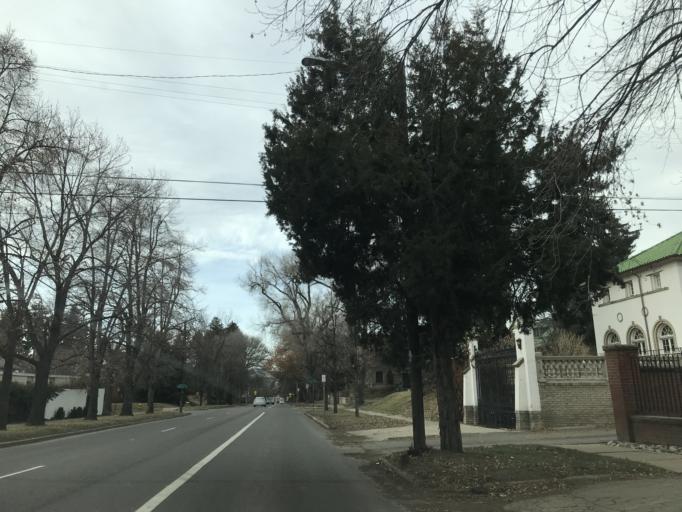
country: US
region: Colorado
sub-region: Denver County
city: Denver
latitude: 39.7292
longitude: -104.9629
